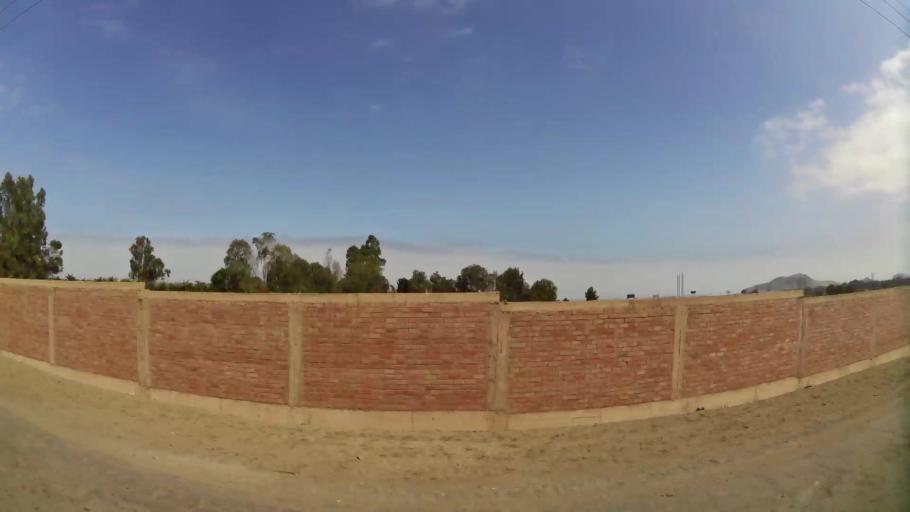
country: PE
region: Lima
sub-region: Provincia de Canete
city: Mala
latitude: -12.7150
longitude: -76.6194
